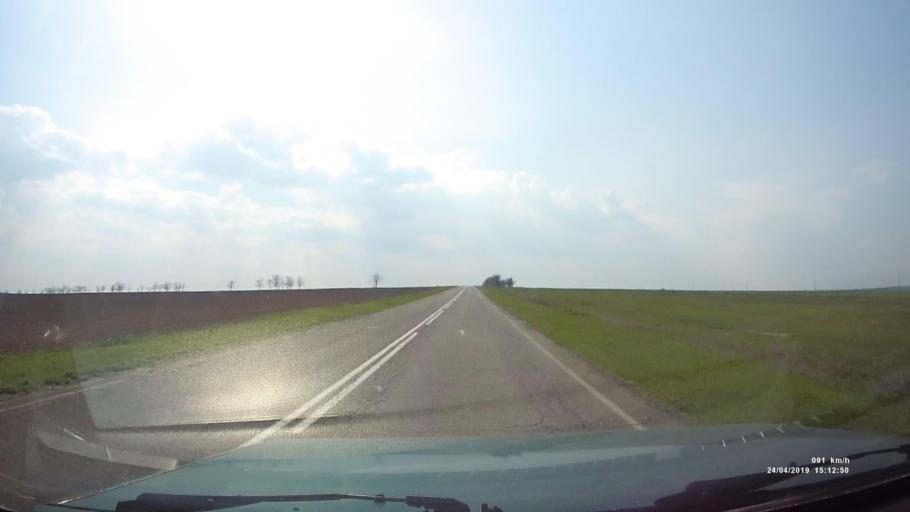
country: RU
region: Rostov
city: Remontnoye
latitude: 46.5464
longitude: 43.2923
